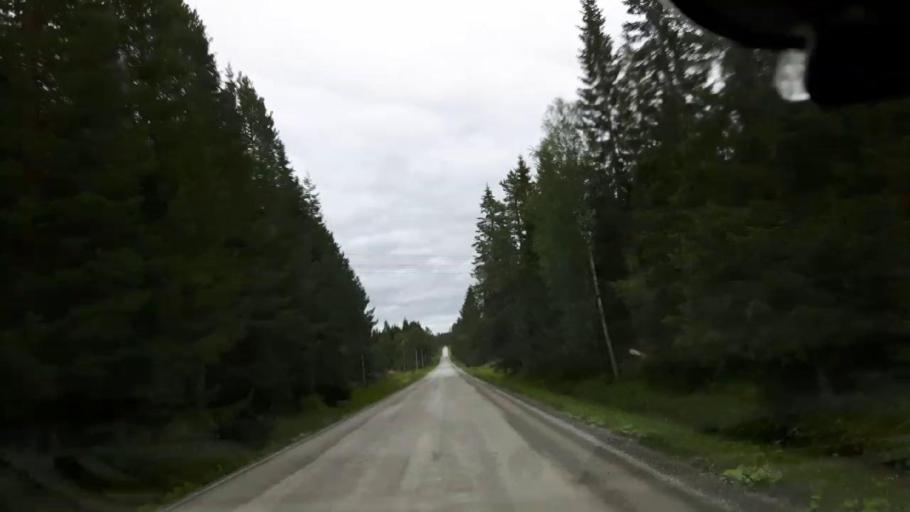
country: SE
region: Jaemtland
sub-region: OEstersunds Kommun
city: Brunflo
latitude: 63.0990
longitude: 15.1187
